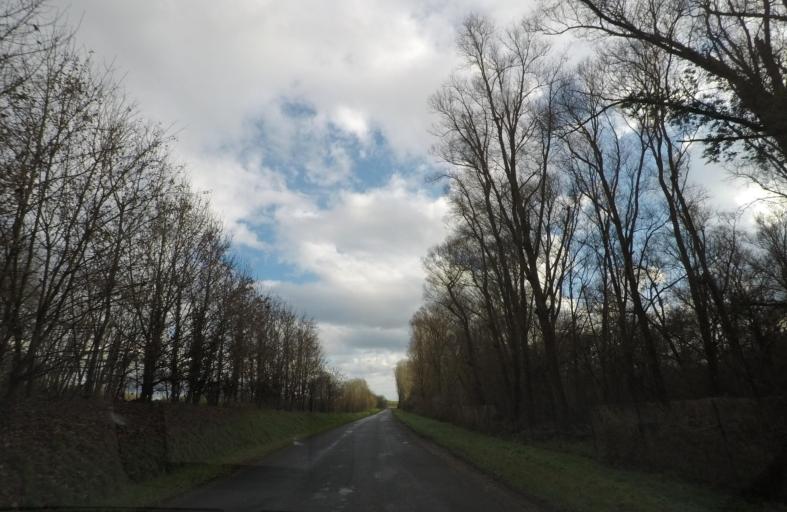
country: FR
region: Centre
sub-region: Departement du Cher
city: Bourges
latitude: 47.0493
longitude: 2.4111
